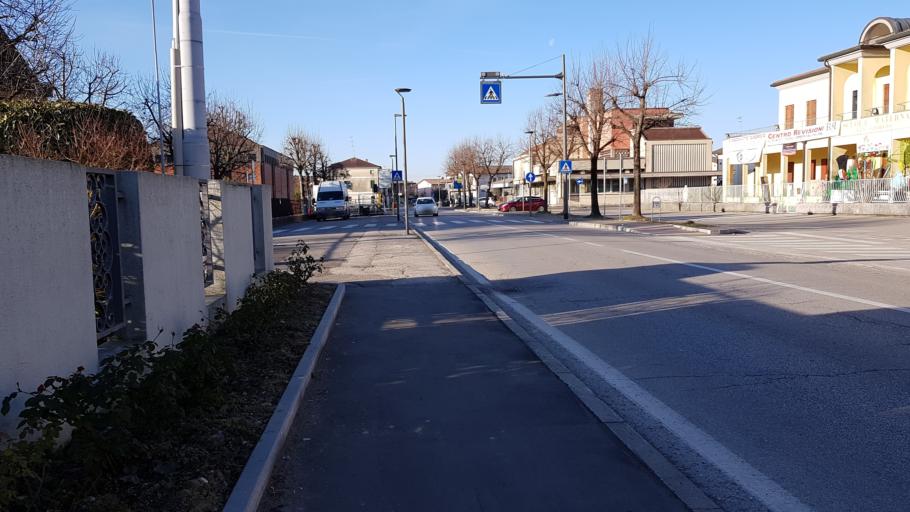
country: IT
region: Veneto
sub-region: Provincia di Padova
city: San Giorgio delle Pertiche
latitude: 45.5411
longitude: 11.9106
